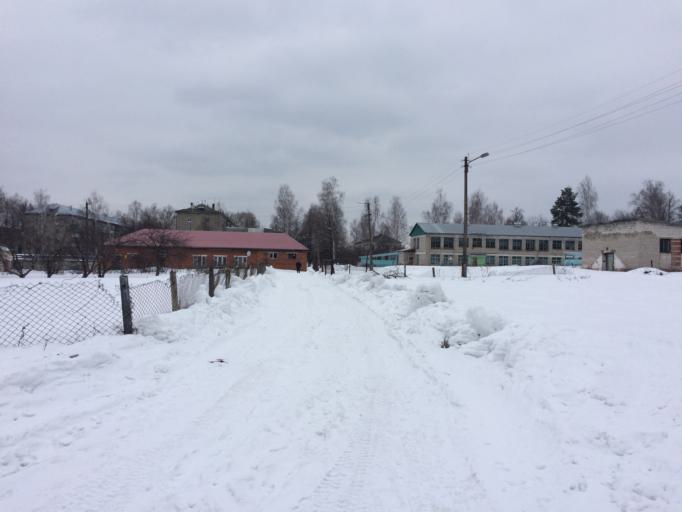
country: RU
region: Mariy-El
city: Mochalishche
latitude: 56.5426
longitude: 48.4066
